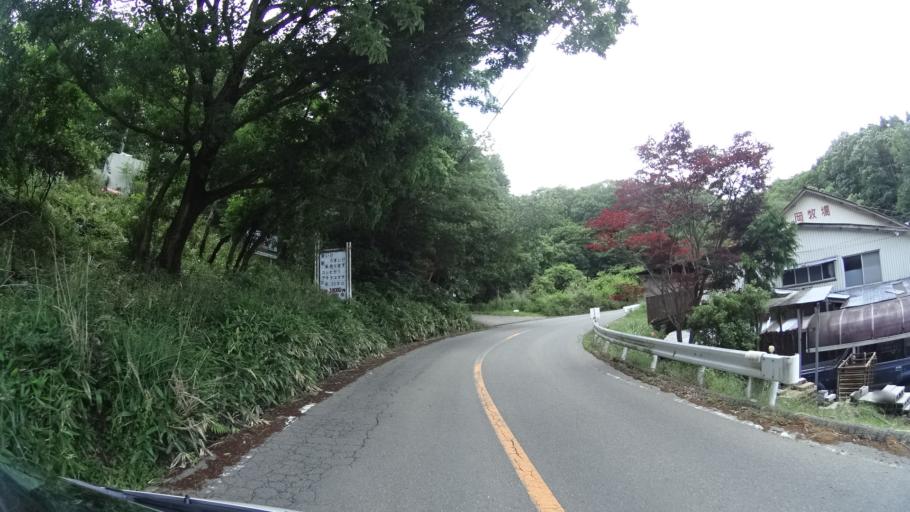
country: JP
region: Hyogo
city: Sasayama
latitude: 35.0269
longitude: 135.3807
